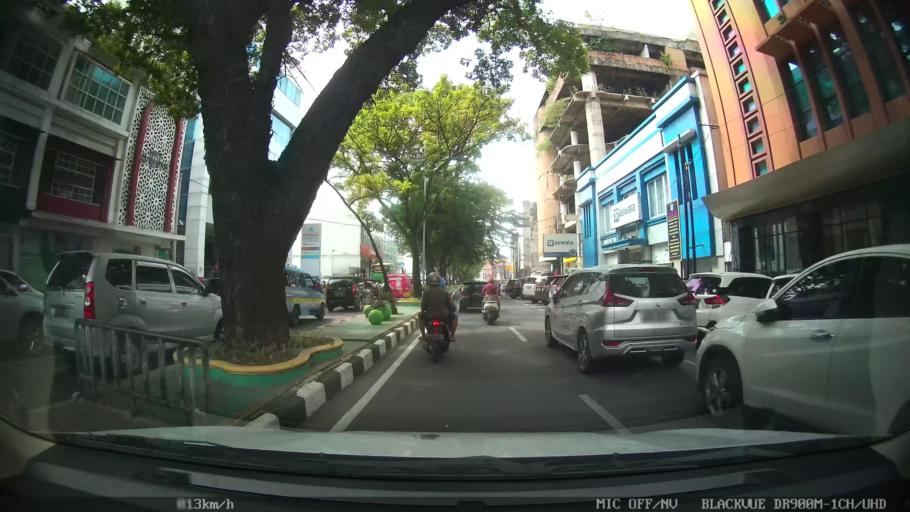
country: ID
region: North Sumatra
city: Medan
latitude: 3.5824
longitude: 98.6819
